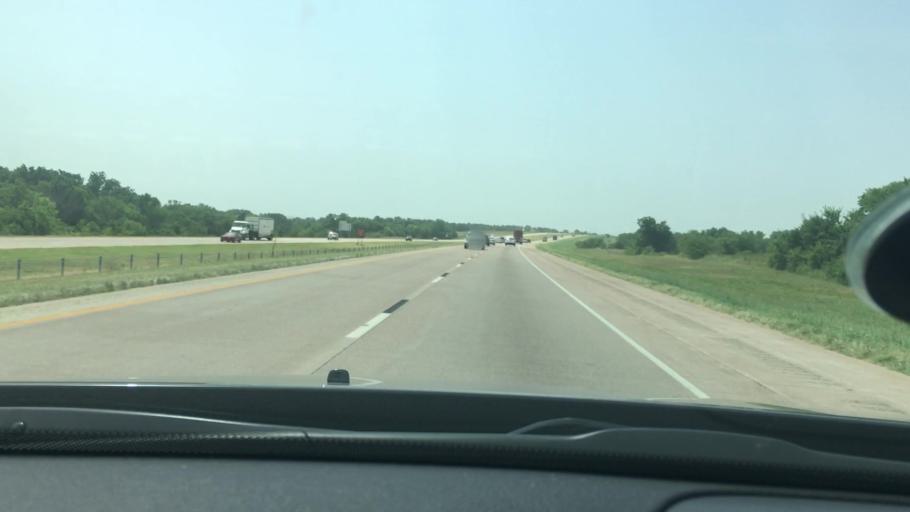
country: US
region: Oklahoma
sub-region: Garvin County
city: Pauls Valley
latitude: 34.6929
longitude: -97.2342
